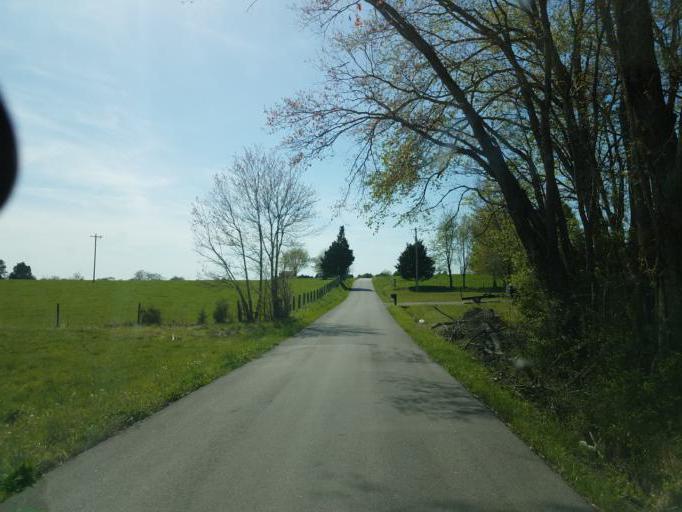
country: US
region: Kentucky
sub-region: Edmonson County
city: Brownsville
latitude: 37.1221
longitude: -86.1432
